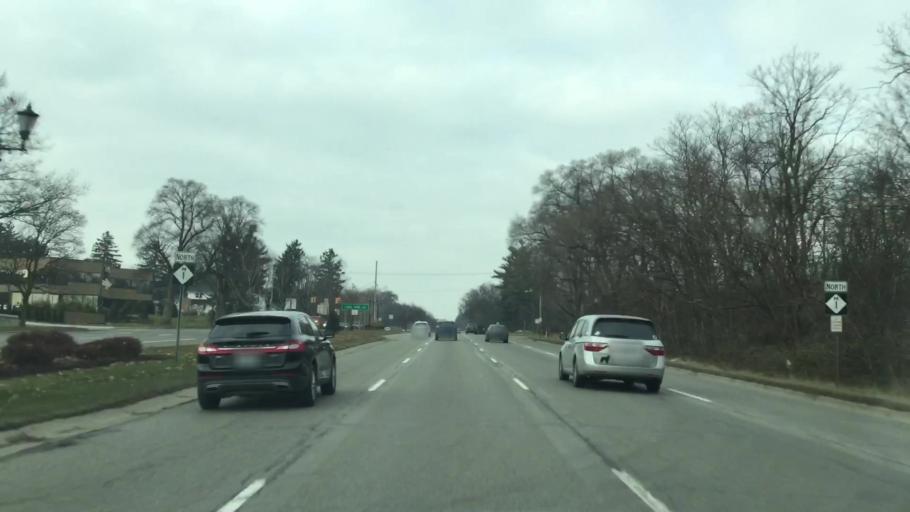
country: US
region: Michigan
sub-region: Oakland County
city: Bloomfield Hills
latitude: 42.5665
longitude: -83.2288
